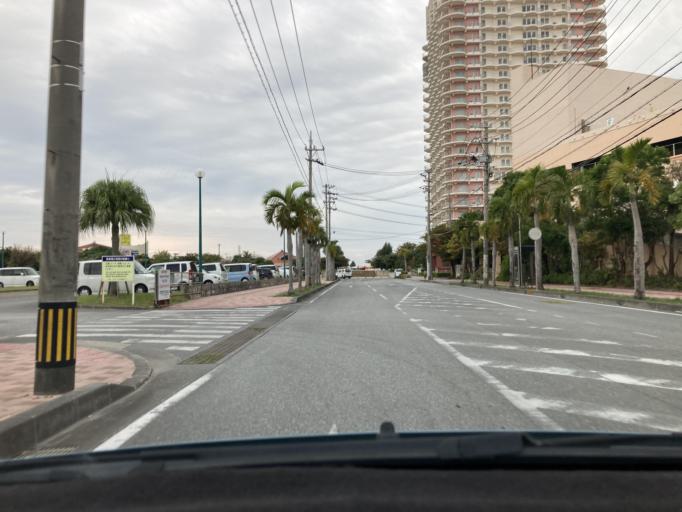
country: JP
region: Okinawa
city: Chatan
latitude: 26.3134
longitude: 127.7578
